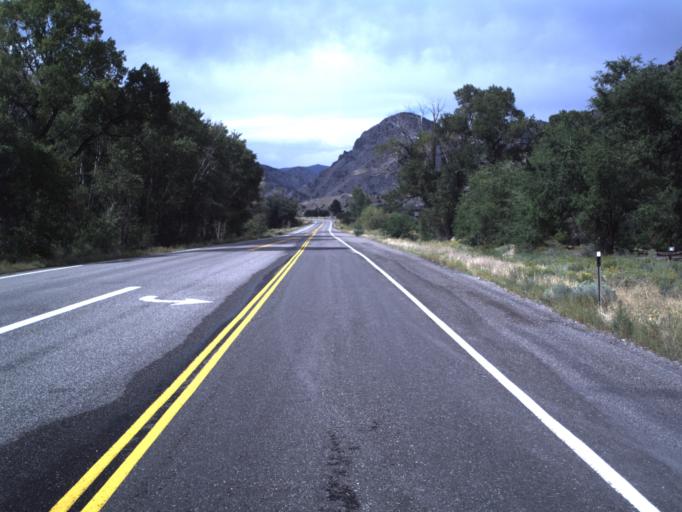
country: US
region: Utah
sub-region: Sevier County
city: Monroe
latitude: 38.5039
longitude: -112.2584
